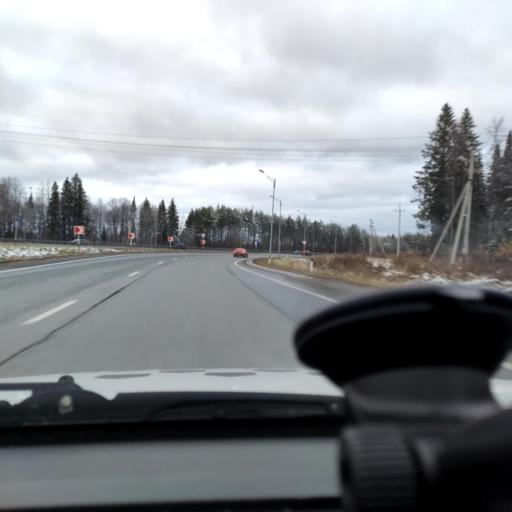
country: RU
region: Perm
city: Ferma
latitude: 58.0016
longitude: 56.3915
